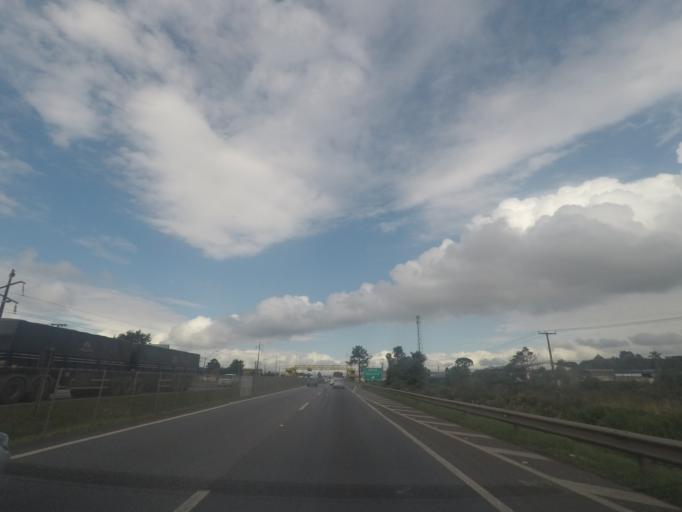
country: BR
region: Parana
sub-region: Piraquara
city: Piraquara
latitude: -25.5217
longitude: -49.1055
